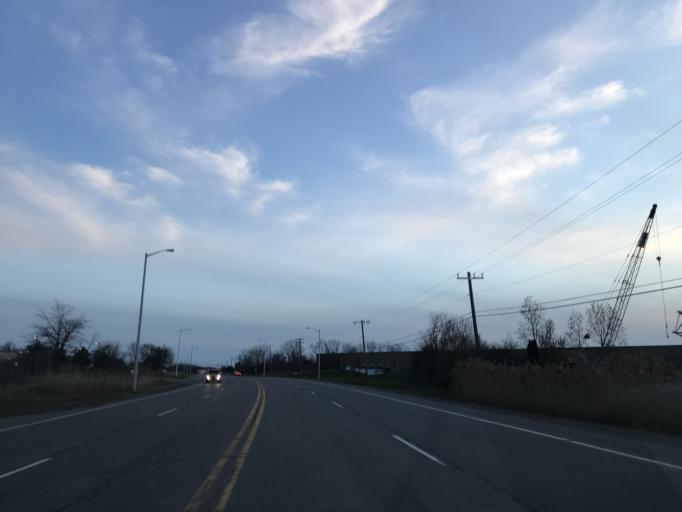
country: US
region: Michigan
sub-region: Wayne County
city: Woodhaven
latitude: 42.1760
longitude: -83.2360
